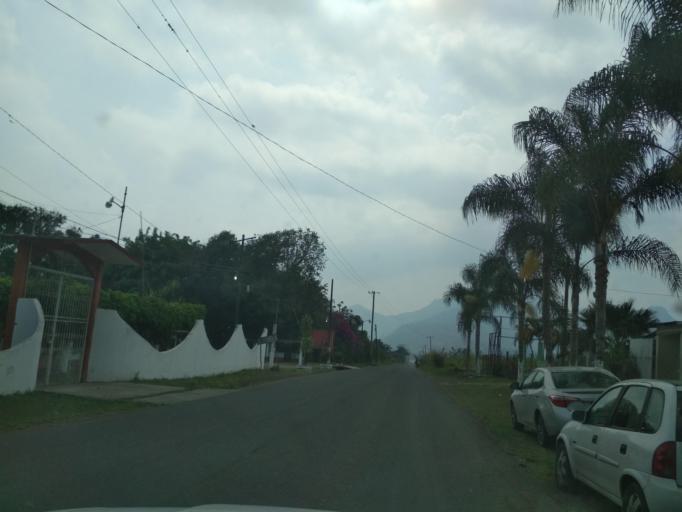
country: MX
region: Veracruz
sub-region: Cordoba
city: San Jose de Tapia
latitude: 18.8496
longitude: -96.9810
